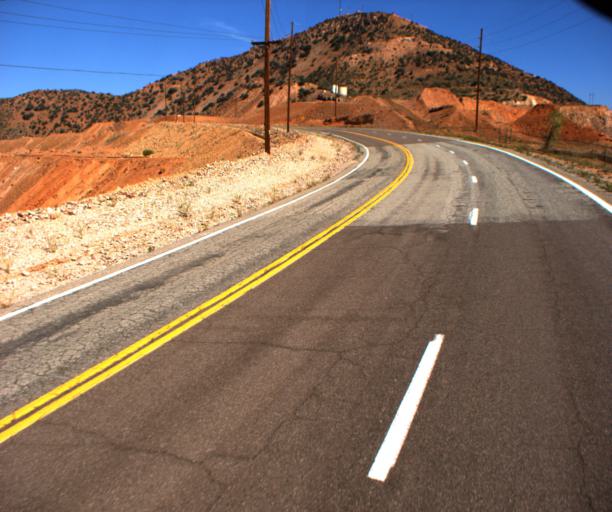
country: US
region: Arizona
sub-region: Greenlee County
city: Morenci
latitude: 33.0849
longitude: -109.3808
